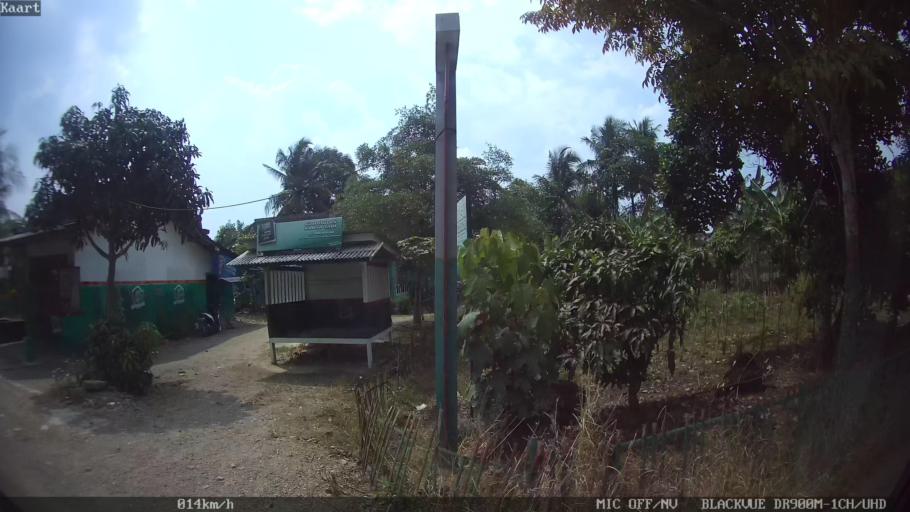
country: ID
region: Lampung
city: Gadingrejo
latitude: -5.3802
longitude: 105.0473
